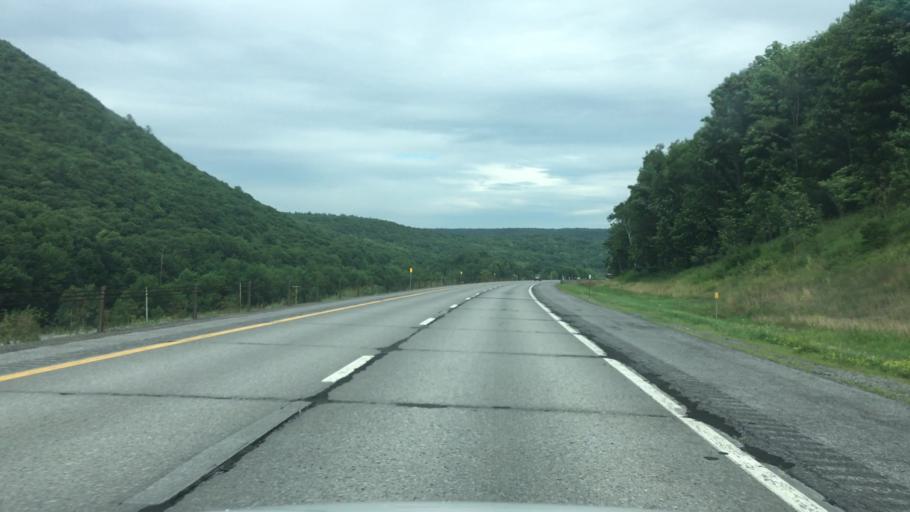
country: US
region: New York
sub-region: Otsego County
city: Worcester
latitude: 42.6466
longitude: -74.6426
